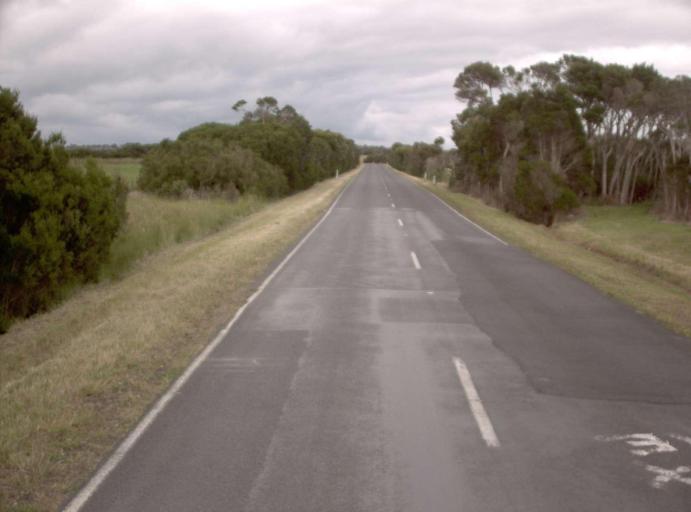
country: AU
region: Victoria
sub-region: Bass Coast
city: North Wonthaggi
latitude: -38.5817
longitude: 145.6253
